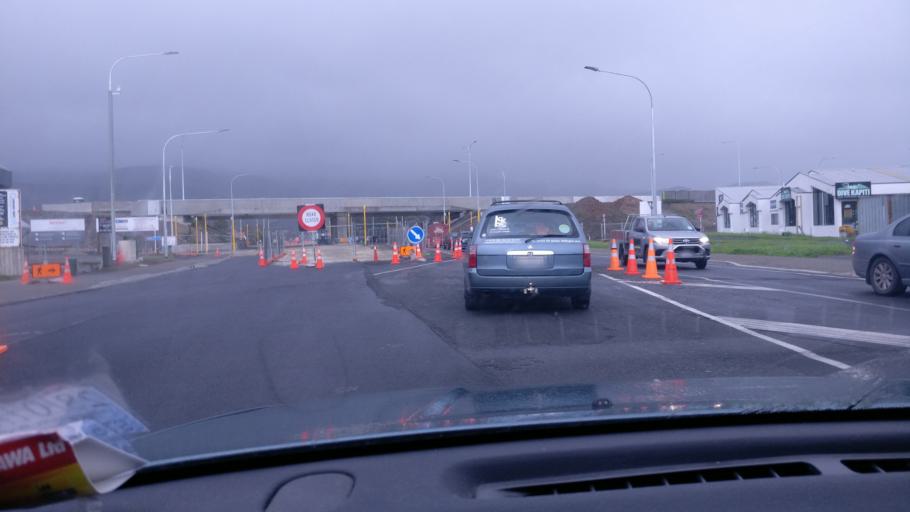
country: NZ
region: Wellington
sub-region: Kapiti Coast District
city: Paraparaumu
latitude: -40.9076
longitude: 174.9989
